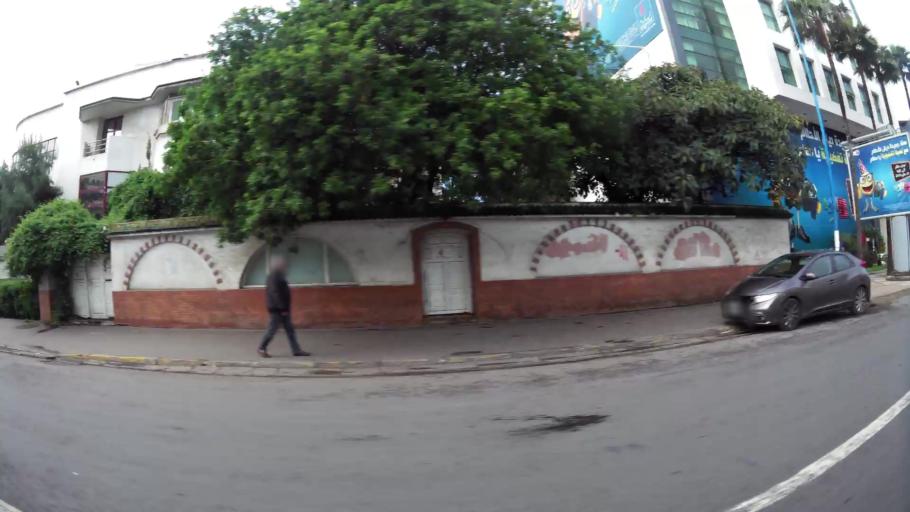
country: MA
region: Grand Casablanca
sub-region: Casablanca
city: Casablanca
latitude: 33.5841
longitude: -7.6270
